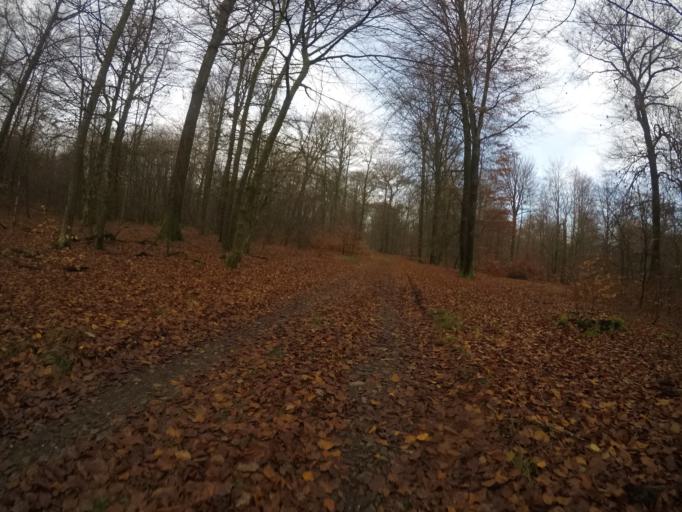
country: BE
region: Wallonia
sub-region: Province du Luxembourg
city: Habay-la-Vieille
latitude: 49.7445
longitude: 5.5933
